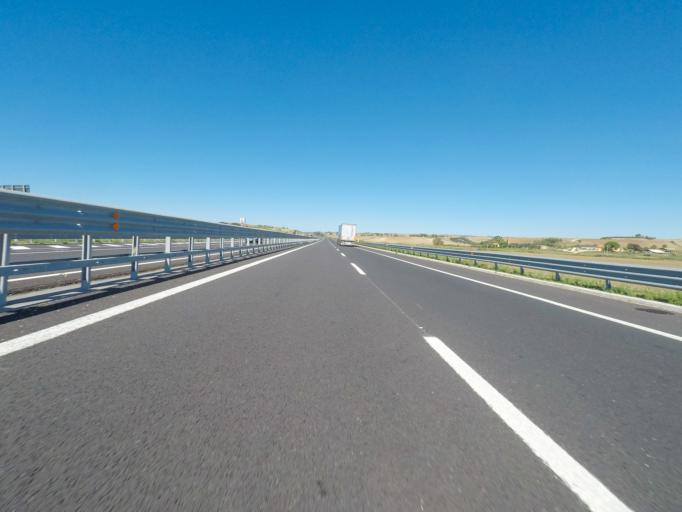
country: IT
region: Latium
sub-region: Citta metropolitana di Roma Capitale
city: Aurelia
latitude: 42.1974
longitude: 11.7857
